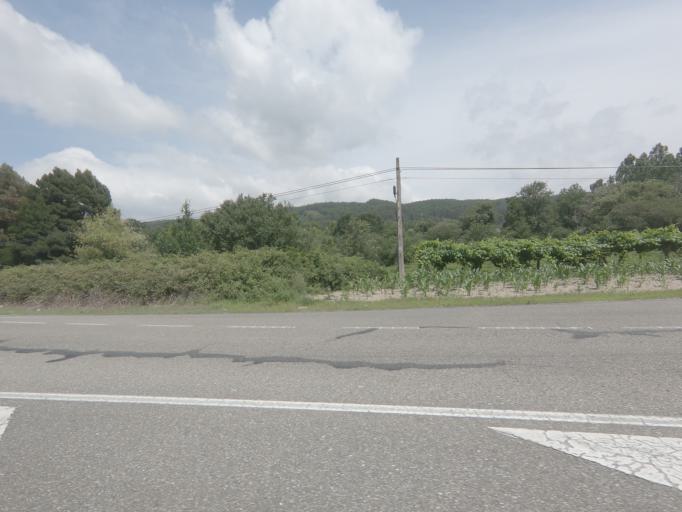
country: ES
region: Galicia
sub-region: Provincia de Pontevedra
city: Tomino
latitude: 42.0299
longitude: -8.7328
